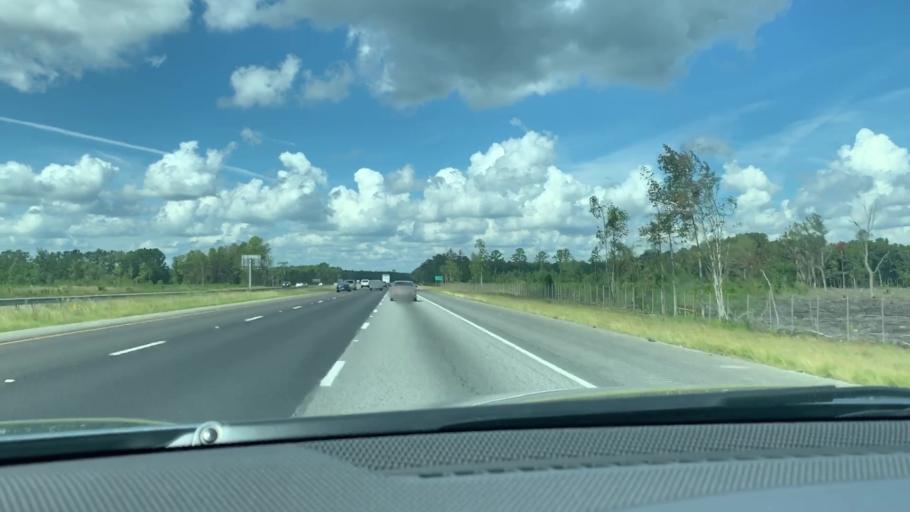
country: US
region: Georgia
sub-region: Camden County
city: Kingsland
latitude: 30.8617
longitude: -81.6792
